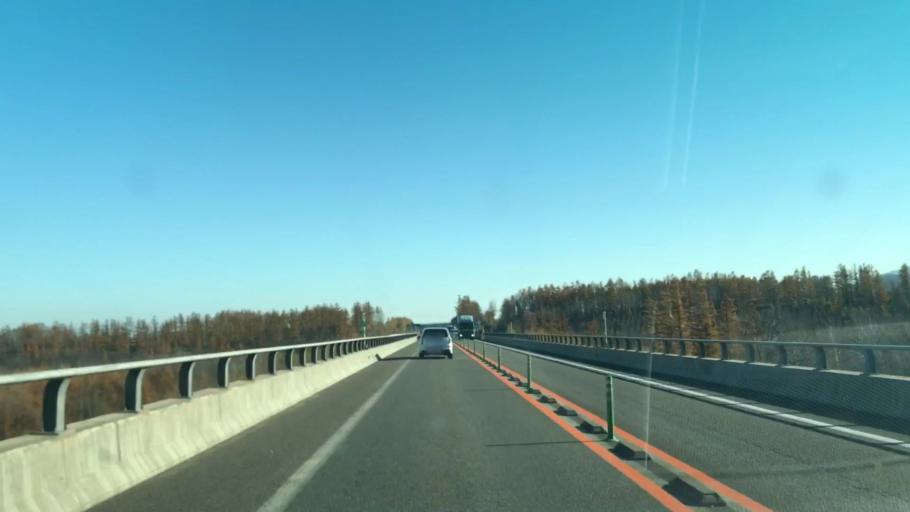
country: JP
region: Hokkaido
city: Otofuke
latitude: 43.0031
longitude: 142.8467
